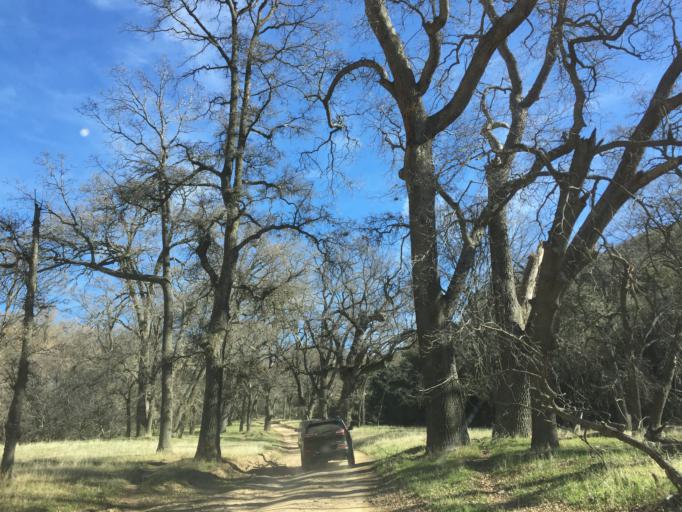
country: US
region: California
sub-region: Kern County
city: Lebec
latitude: 34.8930
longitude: -118.7439
